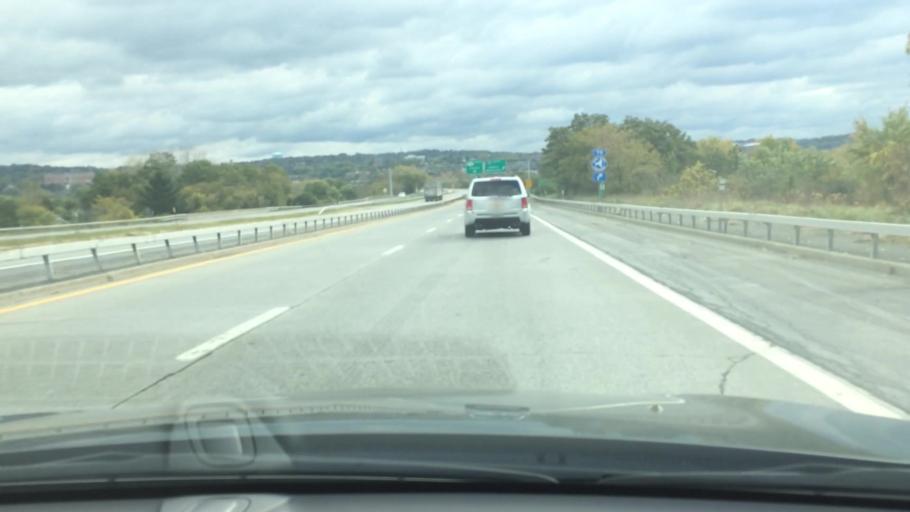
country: US
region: New York
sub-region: Albany County
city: Green Island
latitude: 42.7446
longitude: -73.7028
